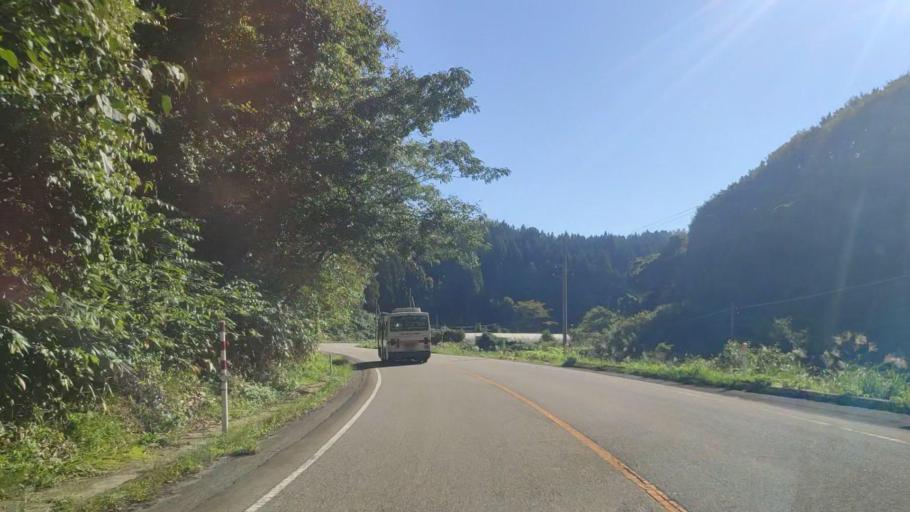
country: JP
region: Ishikawa
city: Nanao
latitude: 37.2434
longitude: 136.9881
